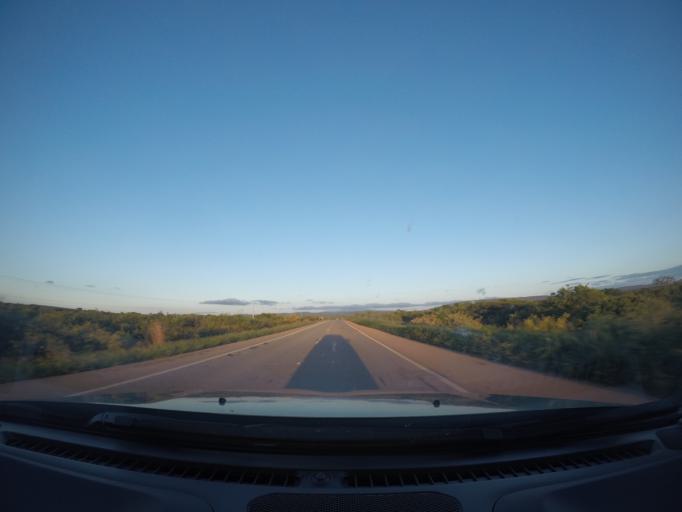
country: BR
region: Bahia
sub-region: Seabra
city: Seabra
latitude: -12.4004
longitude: -41.9438
